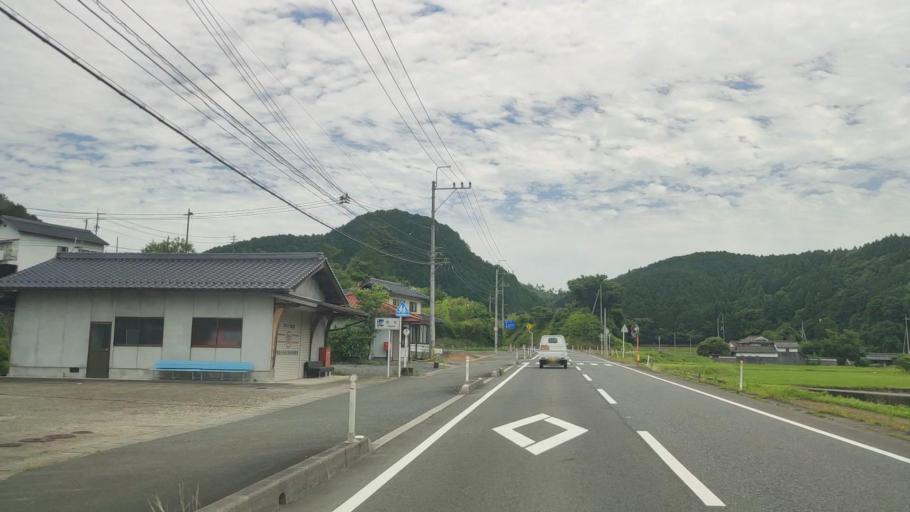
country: JP
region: Okayama
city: Tsuyama
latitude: 35.0626
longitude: 134.2121
